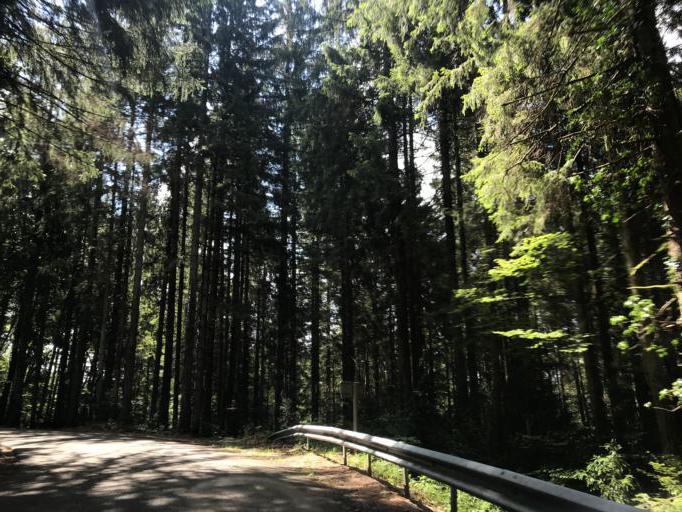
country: FR
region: Franche-Comte
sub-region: Departement du Jura
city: Clairvaux-les-Lacs
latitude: 46.5006
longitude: 5.7698
